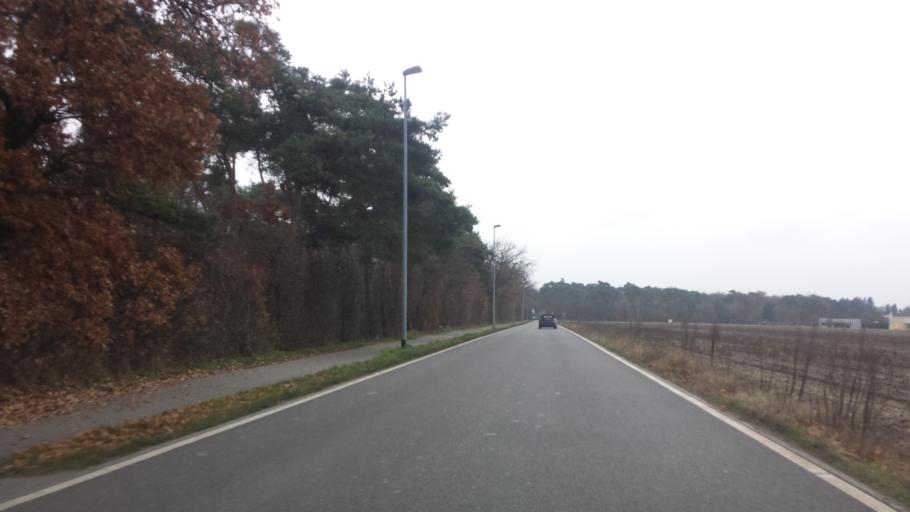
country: DE
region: Hesse
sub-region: Regierungsbezirk Darmstadt
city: Burstadt
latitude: 49.6358
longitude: 8.4803
